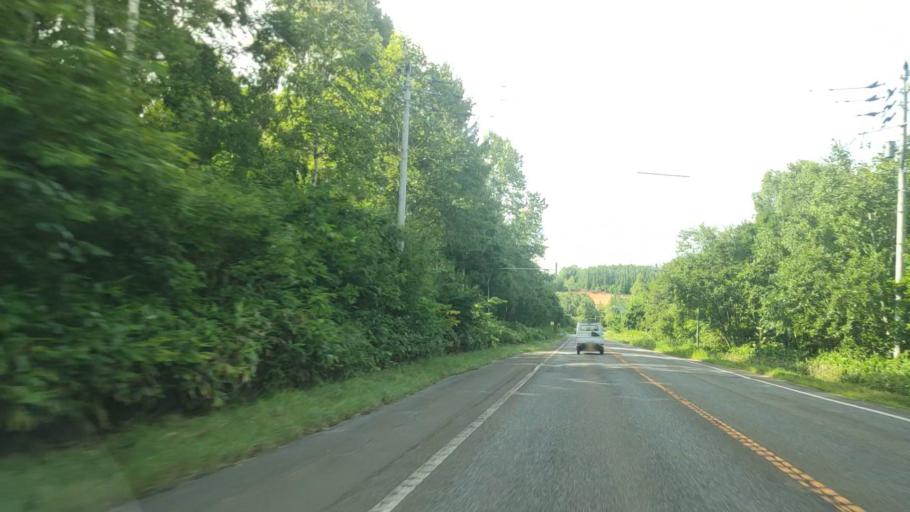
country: JP
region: Hokkaido
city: Nayoro
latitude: 44.3913
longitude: 142.3965
